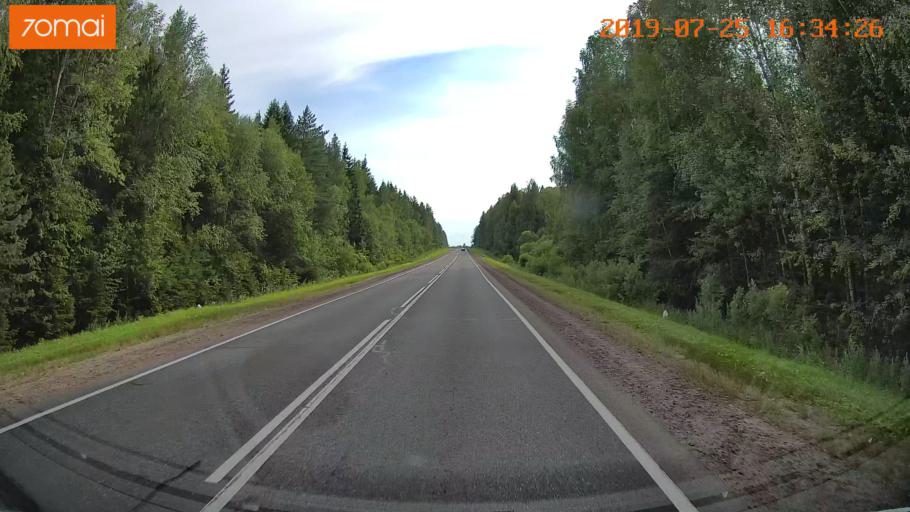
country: RU
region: Ivanovo
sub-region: Privolzhskiy Rayon
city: Ples
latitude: 57.4169
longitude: 41.4374
